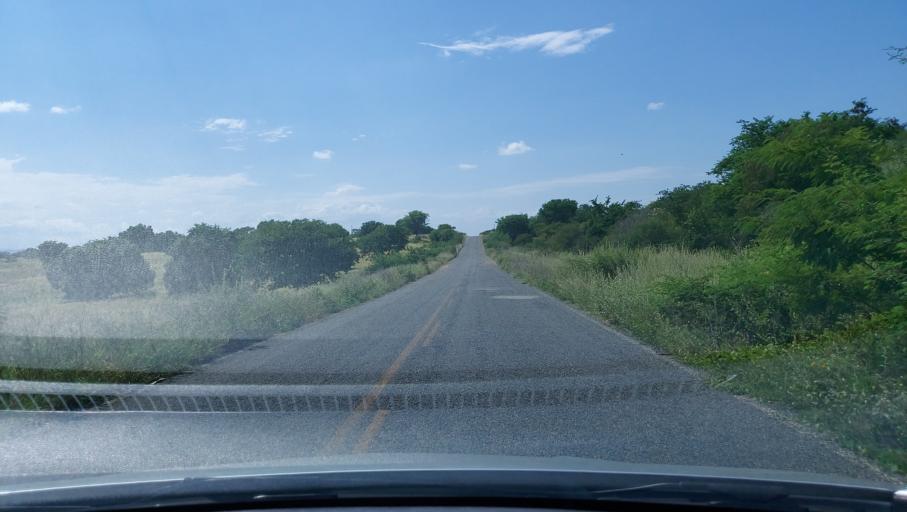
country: BR
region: Bahia
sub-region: Oliveira Dos Brejinhos
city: Beira Rio
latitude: -12.1592
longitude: -42.5503
